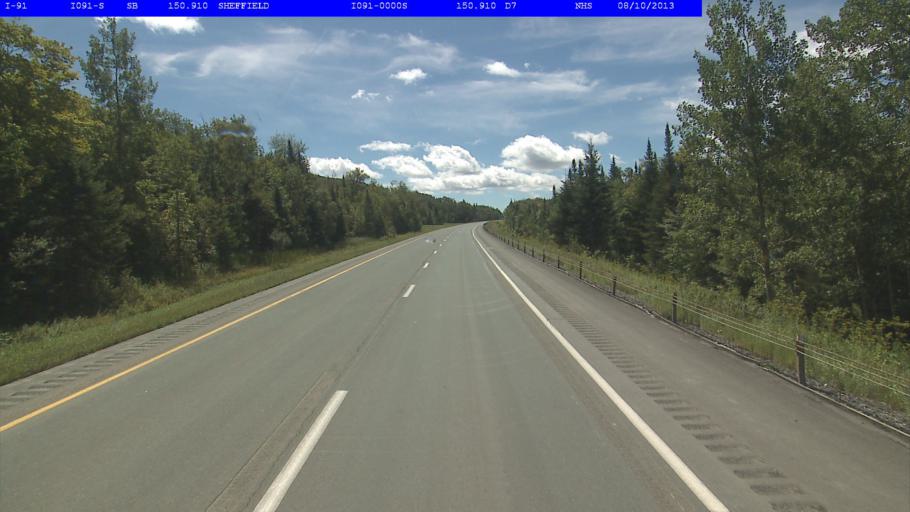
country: US
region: Vermont
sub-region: Caledonia County
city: Lyndonville
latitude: 44.6778
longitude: -72.1330
